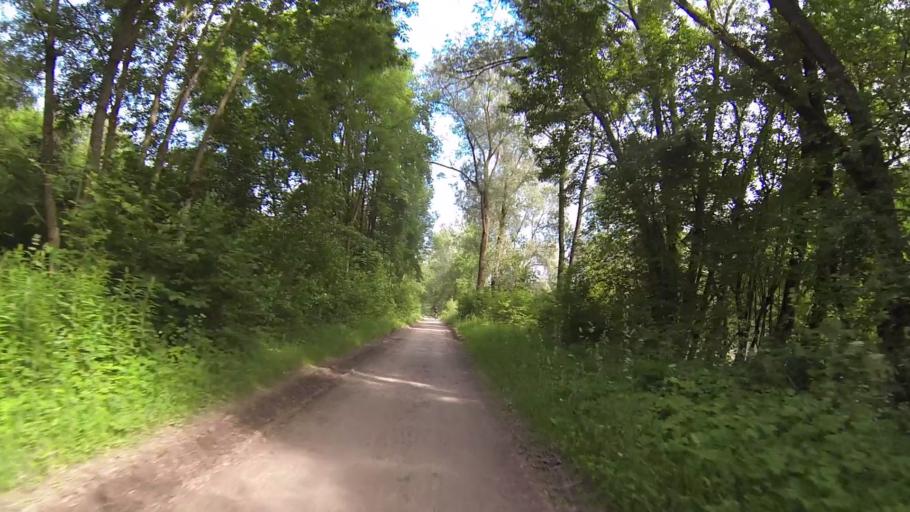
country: DE
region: Bavaria
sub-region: Swabia
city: Senden
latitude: 48.3283
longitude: 10.0204
